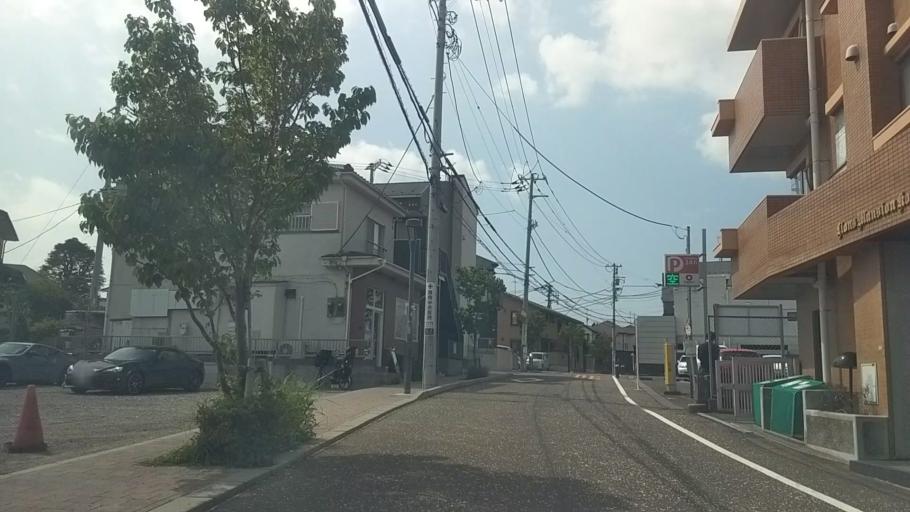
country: JP
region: Kanagawa
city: Yokohama
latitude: 35.3943
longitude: 139.5920
